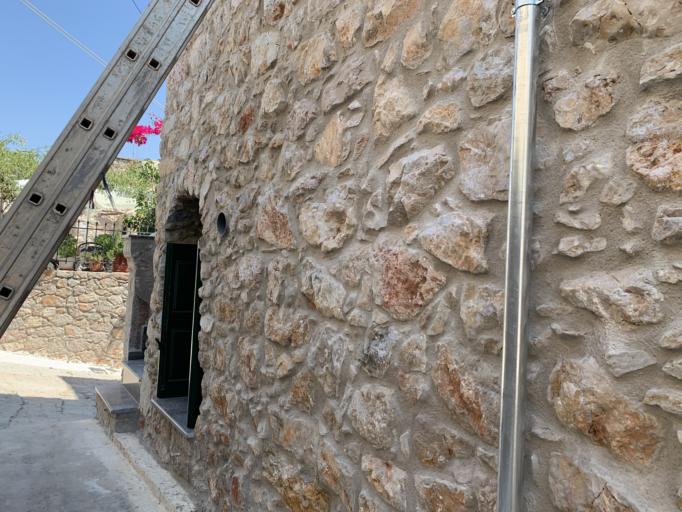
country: GR
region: North Aegean
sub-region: Chios
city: Thymiana
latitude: 38.2968
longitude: 26.0079
